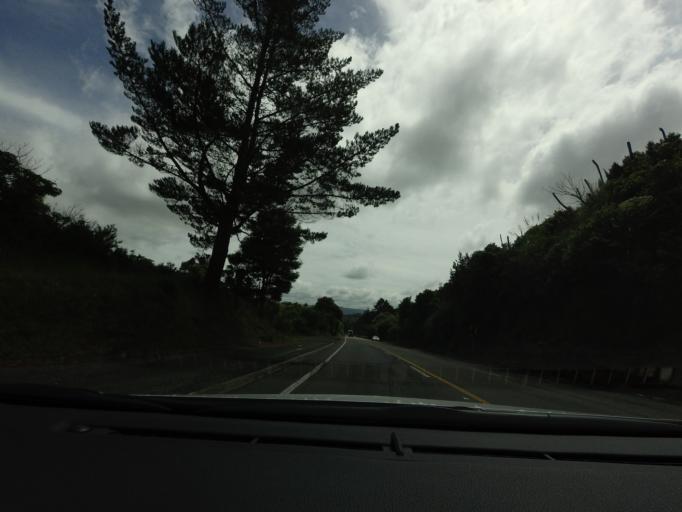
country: NZ
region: Auckland
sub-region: Auckland
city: Warkworth
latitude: -36.4615
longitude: 174.6526
